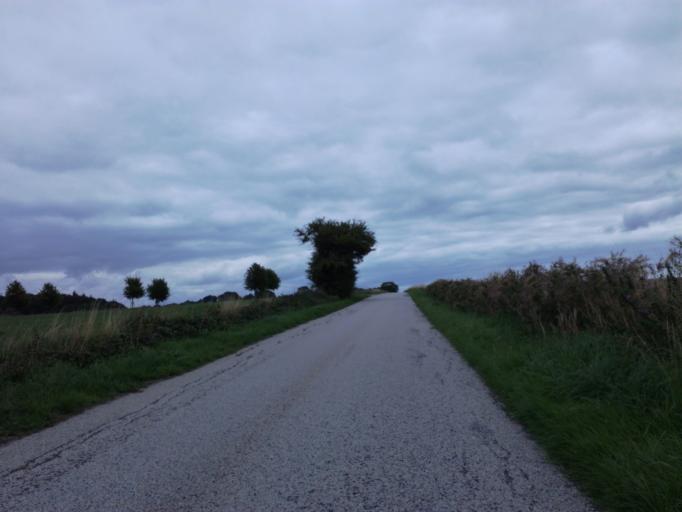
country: DK
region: South Denmark
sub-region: Vejle Kommune
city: Borkop
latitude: 55.6683
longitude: 9.6001
